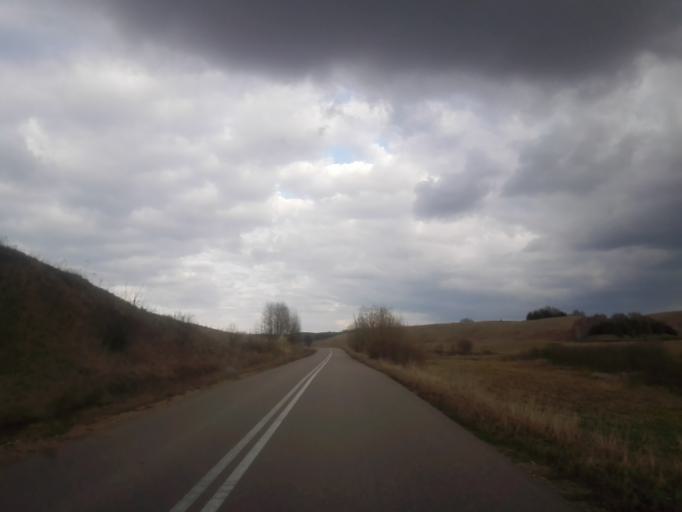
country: PL
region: Podlasie
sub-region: Suwalki
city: Suwalki
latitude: 54.2004
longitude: 22.9817
